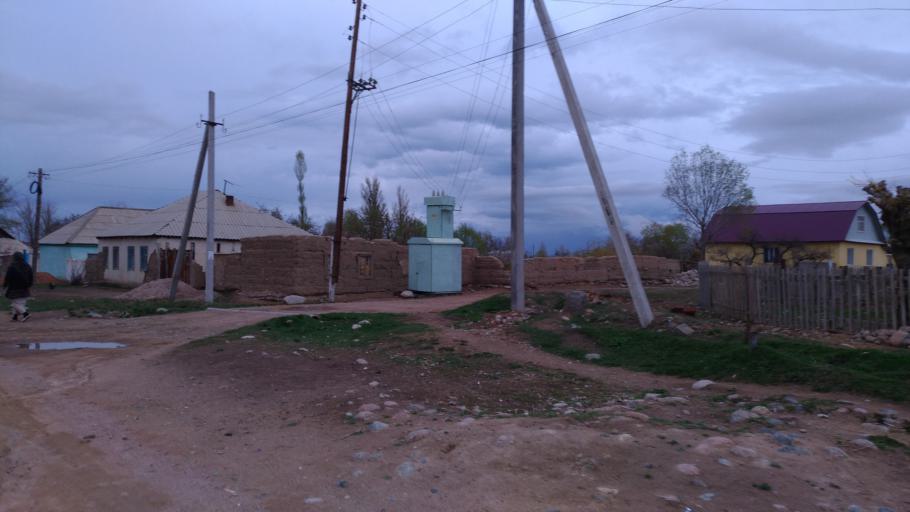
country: KG
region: Ysyk-Koel
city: Bokombayevskoye
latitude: 42.1141
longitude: 76.9836
